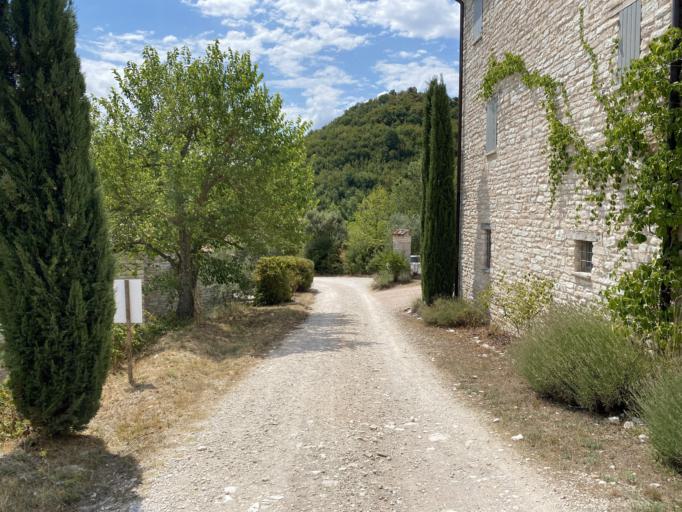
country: IT
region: The Marches
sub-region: Provincia di Pesaro e Urbino
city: Canavaccio
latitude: 43.7045
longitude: 12.7153
